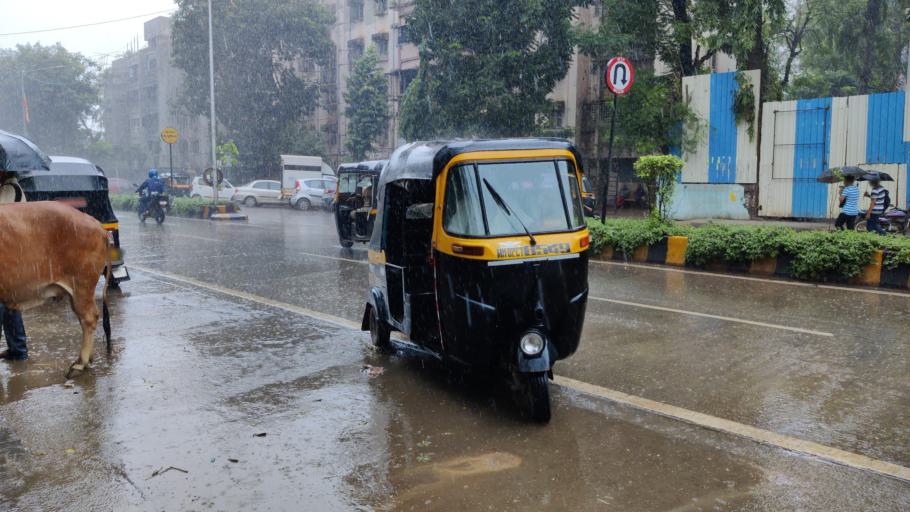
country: IN
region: Maharashtra
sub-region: Mumbai Suburban
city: Borivli
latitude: 19.2439
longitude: 72.8601
